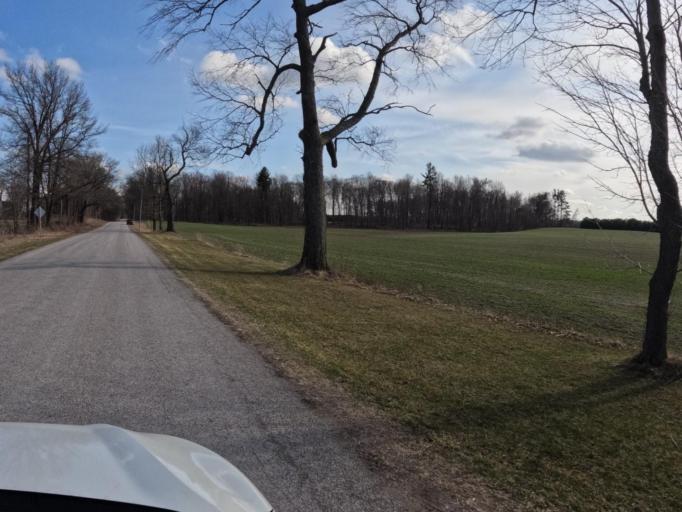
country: CA
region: Ontario
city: Brant
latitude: 43.0038
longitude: -80.4134
